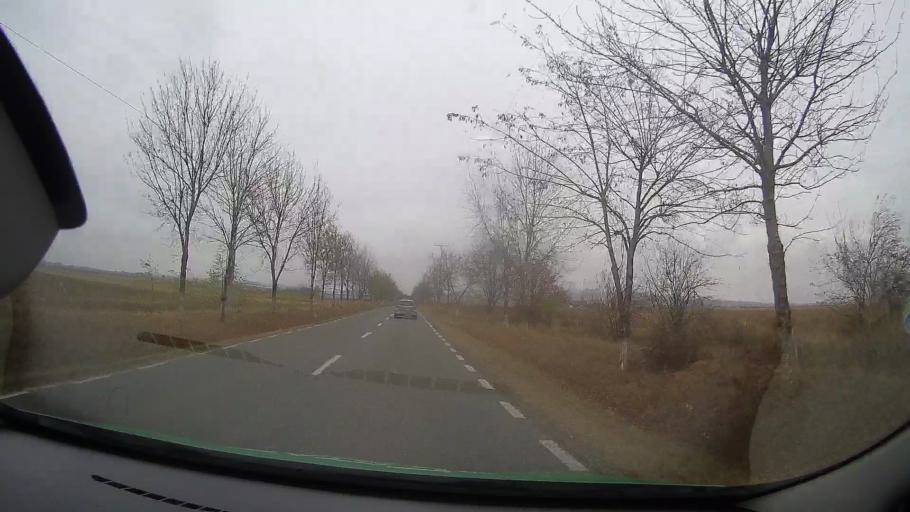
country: RO
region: Prahova
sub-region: Oras Baicoi
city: Liliesti
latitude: 45.0120
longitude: 25.8846
